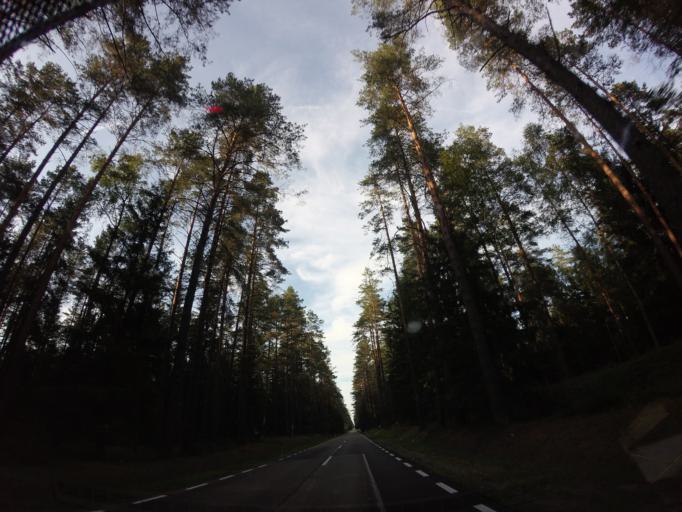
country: PL
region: Podlasie
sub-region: Powiat augustowski
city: Augustow
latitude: 53.9128
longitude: 23.1430
